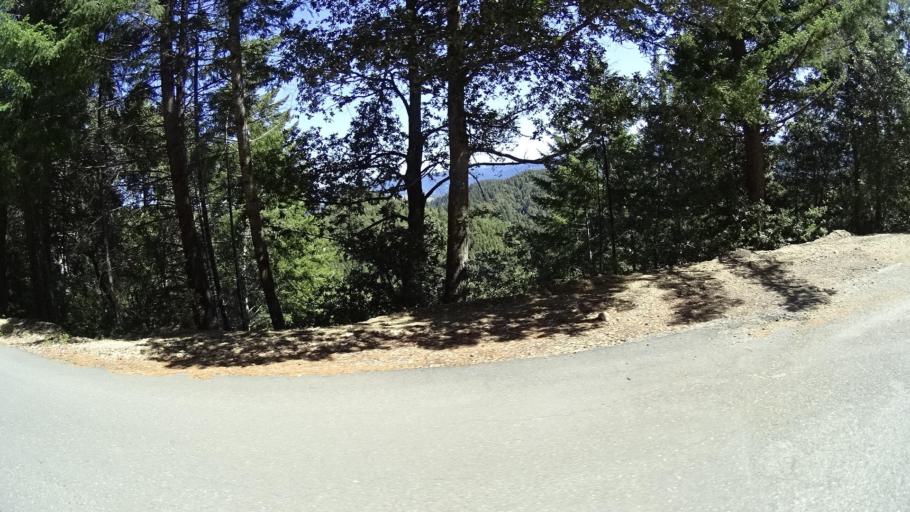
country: US
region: California
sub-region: Humboldt County
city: Redway
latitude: 40.1582
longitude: -124.0770
